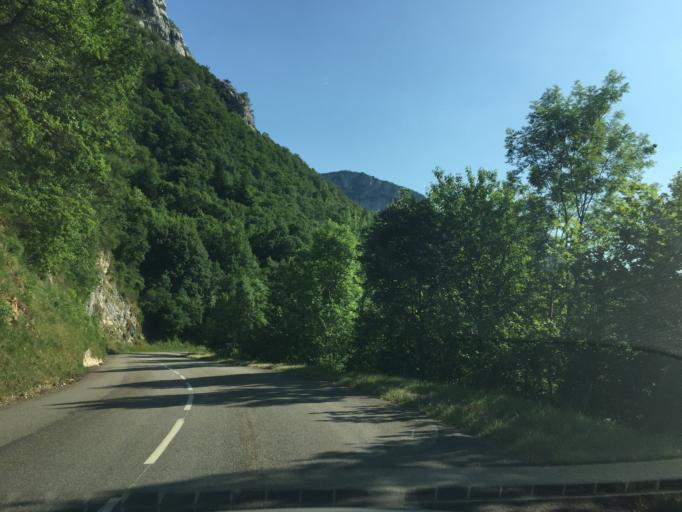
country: FR
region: Rhone-Alpes
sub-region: Departement de la Drome
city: Saint-Laurent-en-Royans
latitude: 45.0235
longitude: 5.3372
